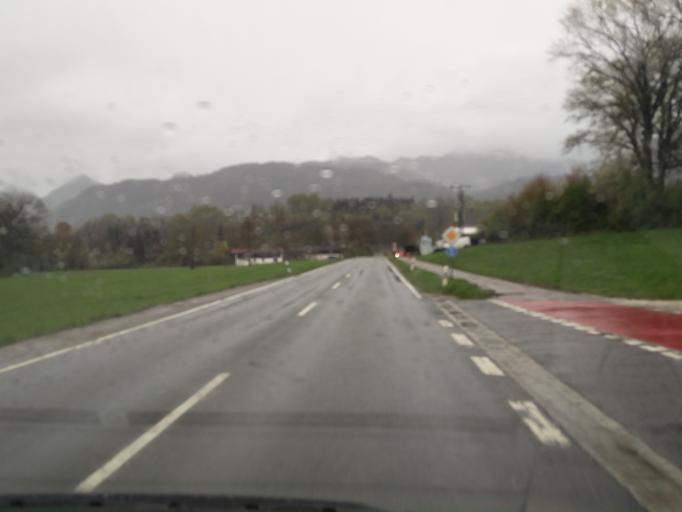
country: DE
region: Bavaria
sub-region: Upper Bavaria
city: Bernau am Chiemsee
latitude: 47.8197
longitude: 12.3620
